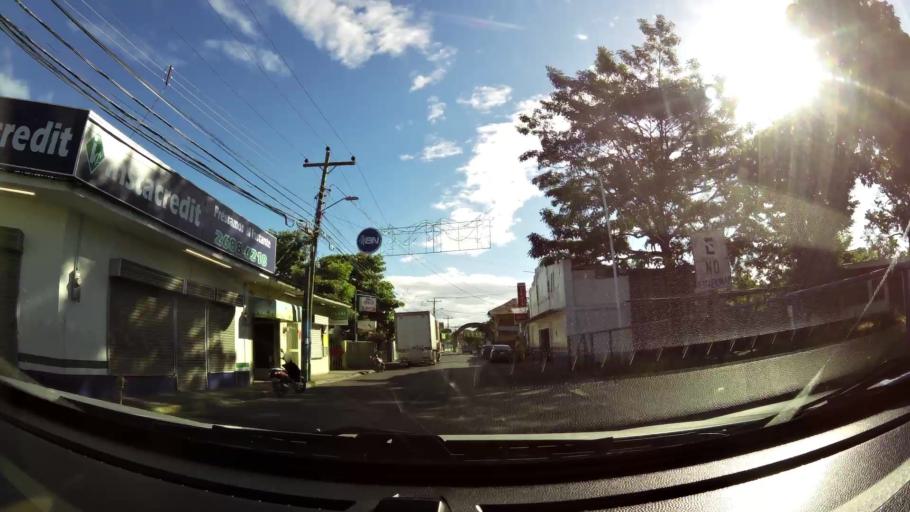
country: CR
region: Guanacaste
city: Belen
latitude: 10.4452
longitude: -85.5520
